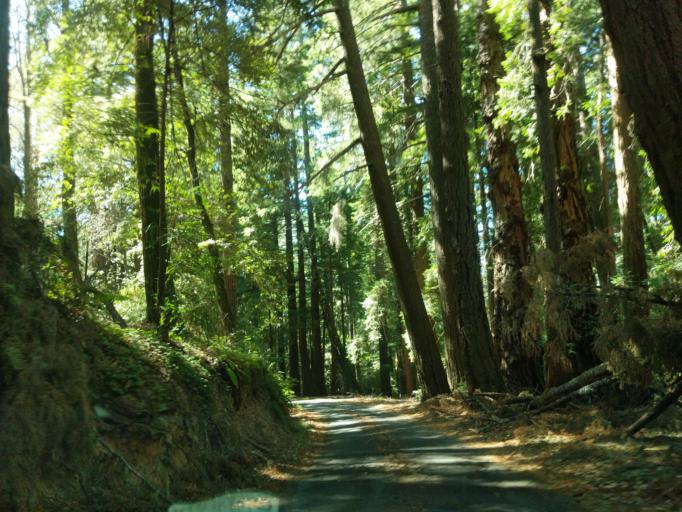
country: US
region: California
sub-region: Sonoma County
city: Monte Rio
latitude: 38.5250
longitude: -123.2369
